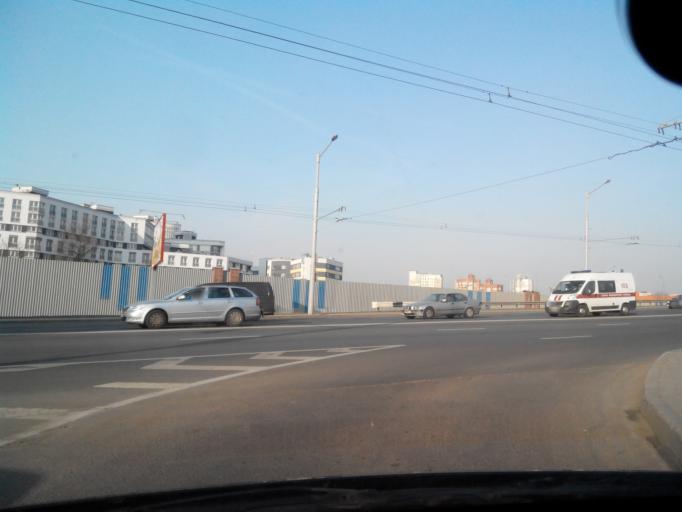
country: BY
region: Minsk
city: Minsk
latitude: 53.9071
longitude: 27.5205
